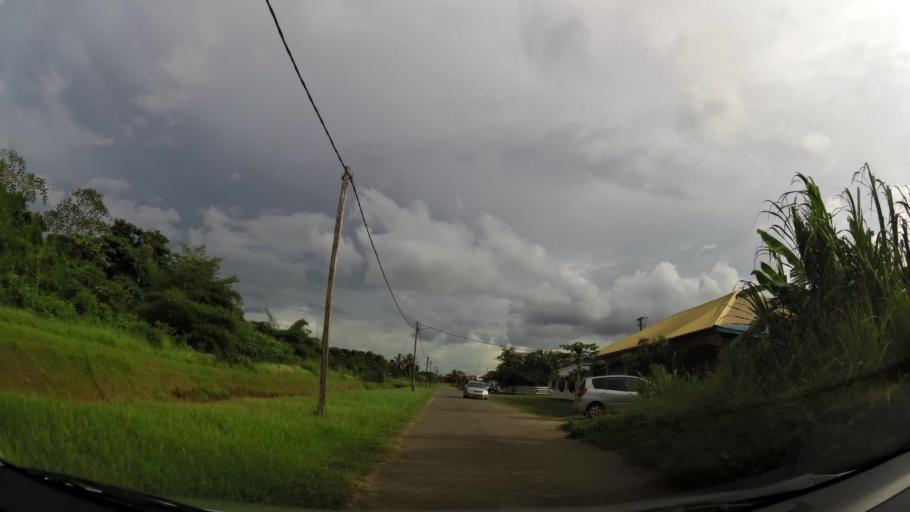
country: SR
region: Paramaribo
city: Paramaribo
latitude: 5.8483
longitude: -55.1773
